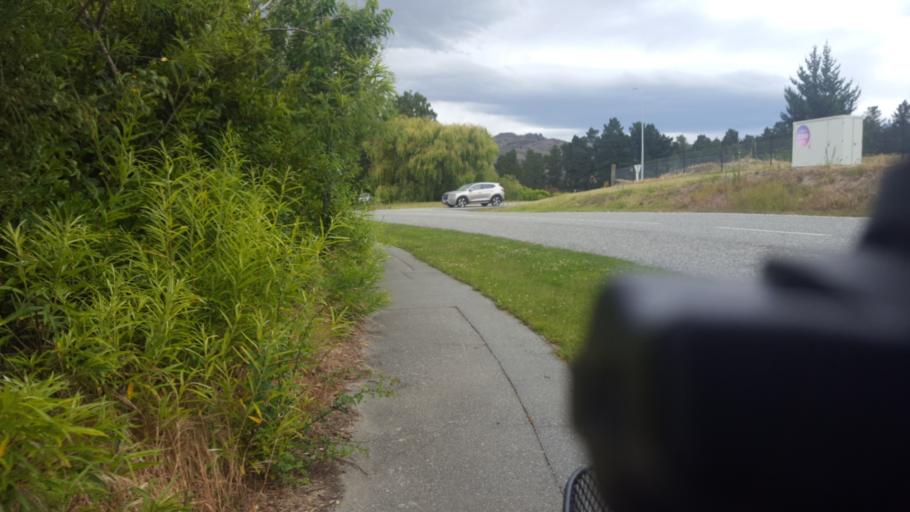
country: NZ
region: Otago
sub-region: Queenstown-Lakes District
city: Wanaka
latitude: -45.2636
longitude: 169.3773
